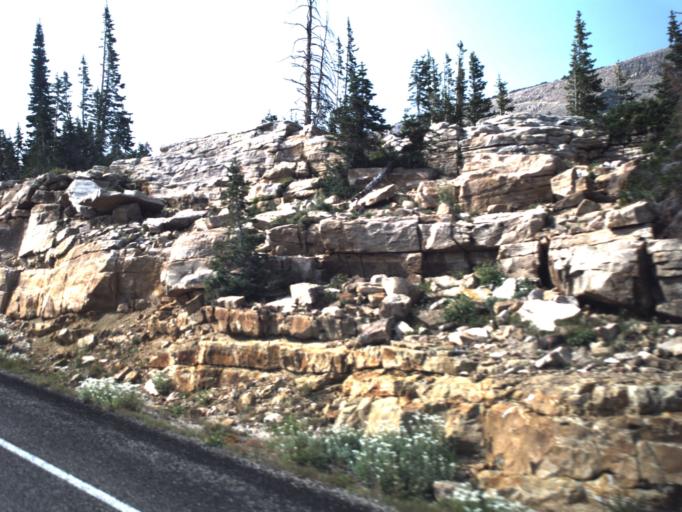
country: US
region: Utah
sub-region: Summit County
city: Kamas
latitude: 40.6861
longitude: -110.9045
